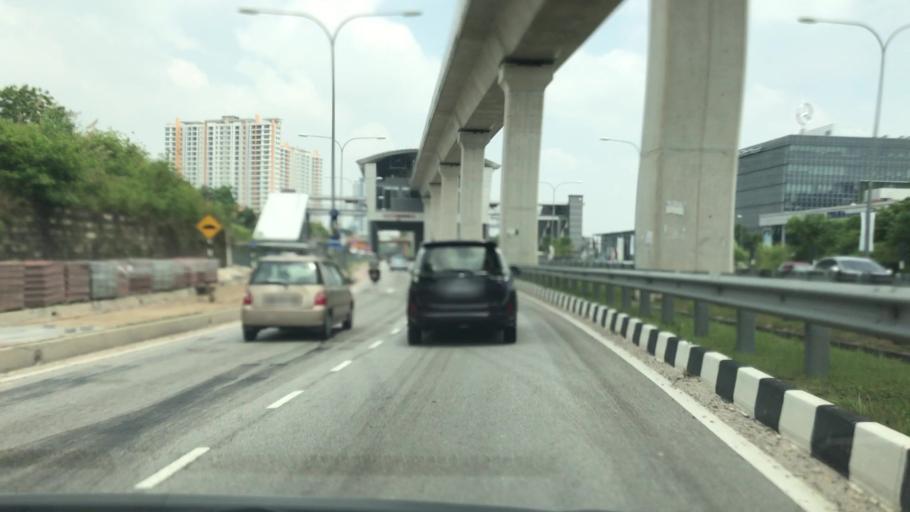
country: MY
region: Selangor
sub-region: Petaling
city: Petaling Jaya
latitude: 3.0555
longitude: 101.6585
